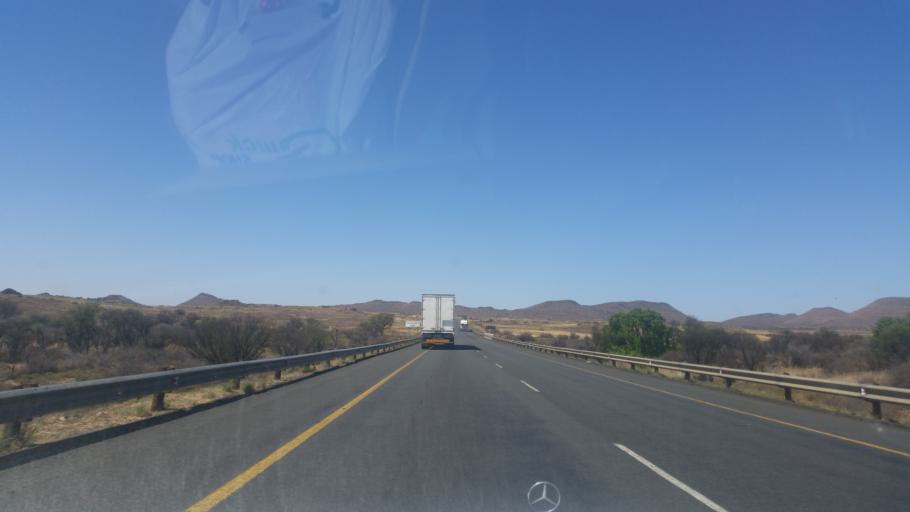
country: ZA
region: Northern Cape
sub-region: Pixley ka Seme District Municipality
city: Colesberg
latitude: -30.6199
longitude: 25.3514
